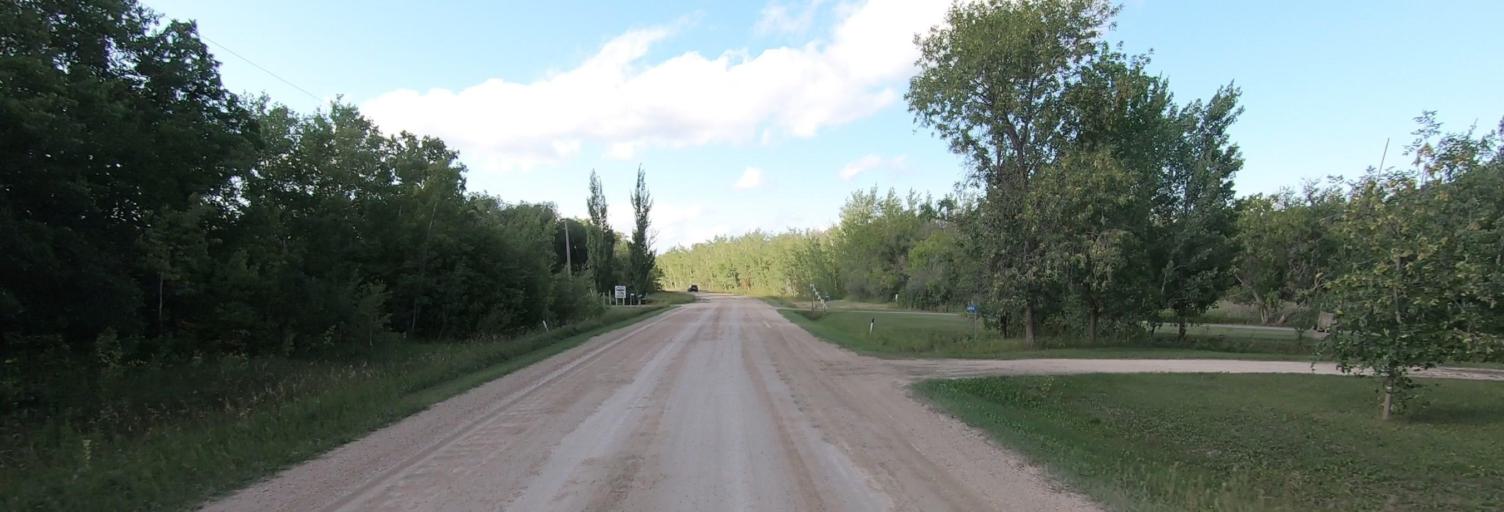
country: CA
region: Manitoba
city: Selkirk
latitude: 50.2300
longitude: -96.8400
